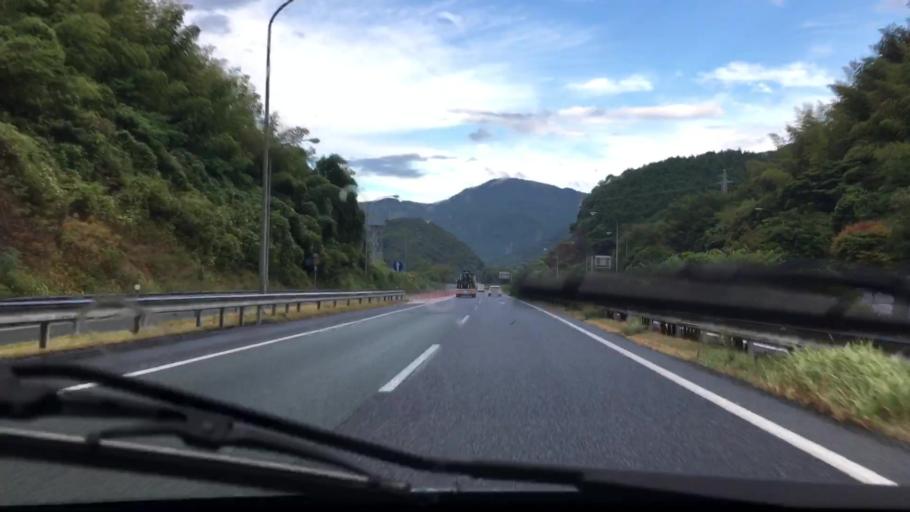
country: JP
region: Fukuoka
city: Kitakyushu
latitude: 33.8033
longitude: 130.8541
